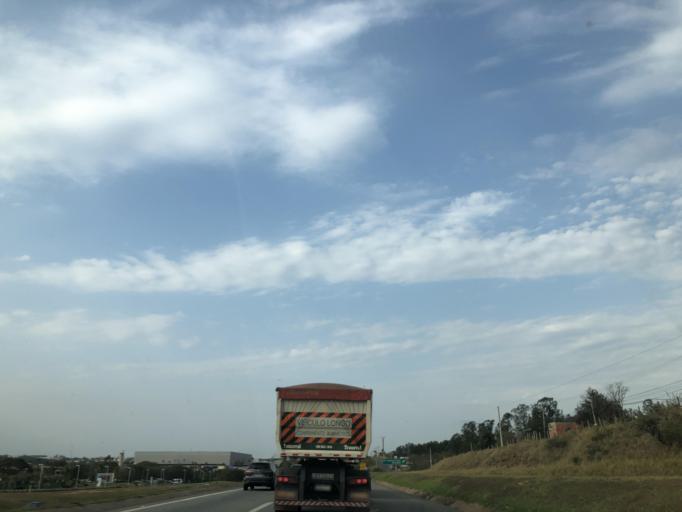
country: BR
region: Sao Paulo
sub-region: Sorocaba
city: Sorocaba
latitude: -23.4283
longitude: -47.3631
